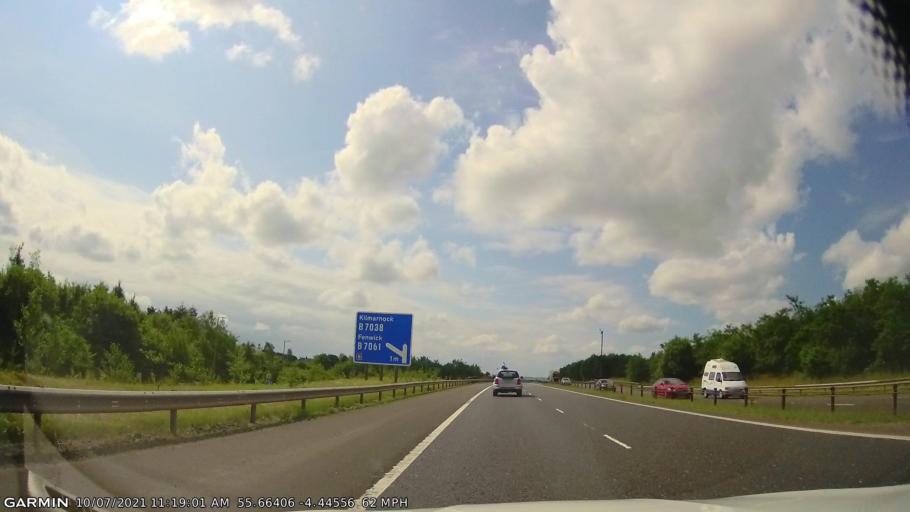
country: GB
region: Scotland
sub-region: East Ayrshire
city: Stewarton
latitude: 55.6641
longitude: -4.4458
